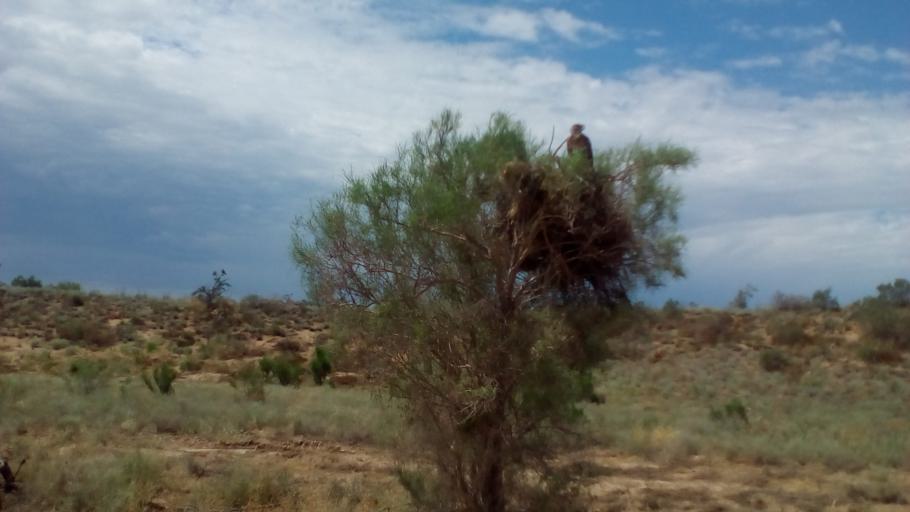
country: KZ
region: Ongtustik Qazaqstan
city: Sholaqqkorghan
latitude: 44.5432
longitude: 69.1951
